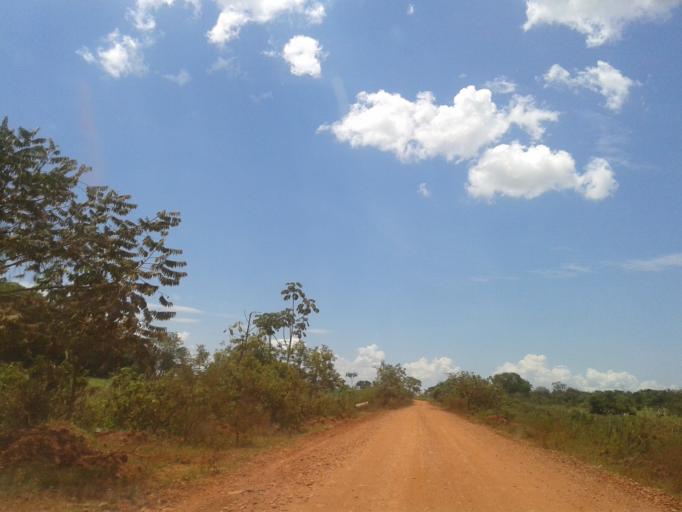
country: BR
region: Minas Gerais
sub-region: Santa Vitoria
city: Santa Vitoria
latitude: -19.1778
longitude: -50.4043
